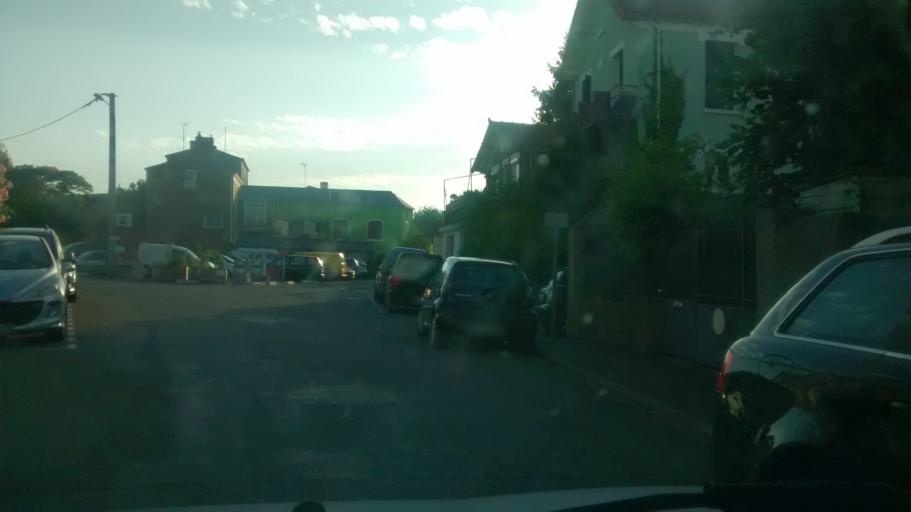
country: FR
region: Pays de la Loire
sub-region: Departement de la Loire-Atlantique
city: Reze
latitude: 47.1937
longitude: -1.5824
